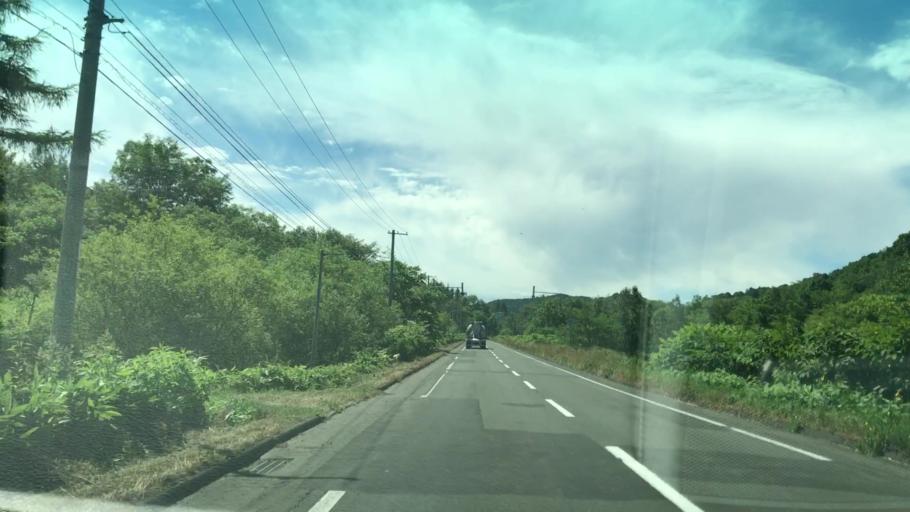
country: JP
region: Hokkaido
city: Shimo-furano
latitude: 42.9372
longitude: 142.4450
